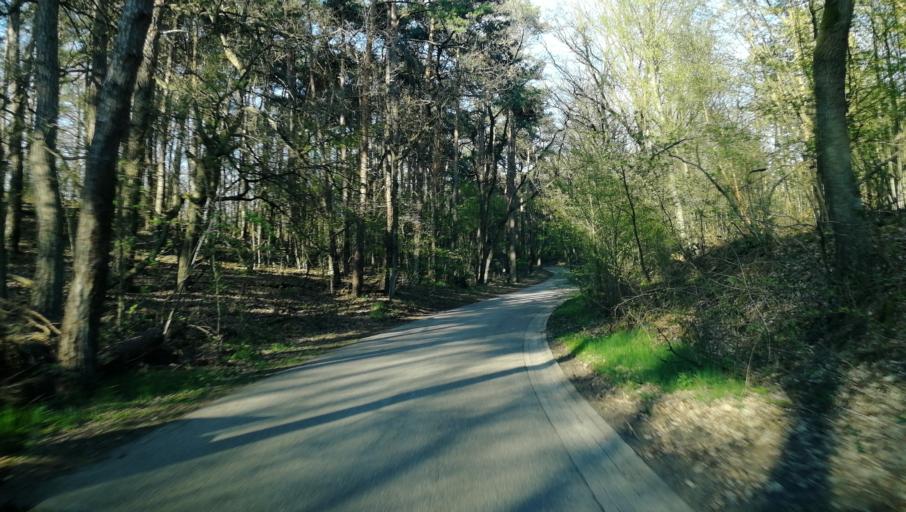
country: NL
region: Limburg
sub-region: Gemeente Venlo
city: Tegelen
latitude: 51.3072
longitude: 6.1483
